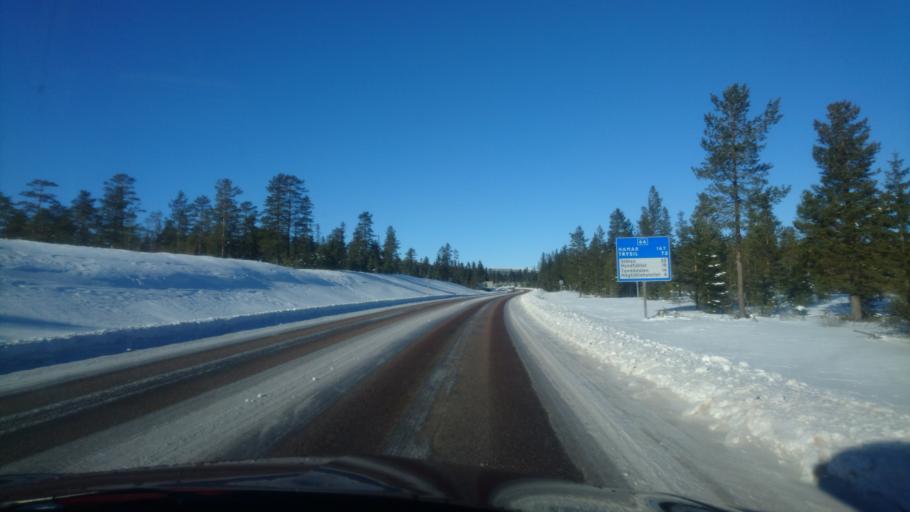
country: SE
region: Dalarna
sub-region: Malung-Saelens kommun
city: Malung
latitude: 61.1664
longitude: 13.1950
